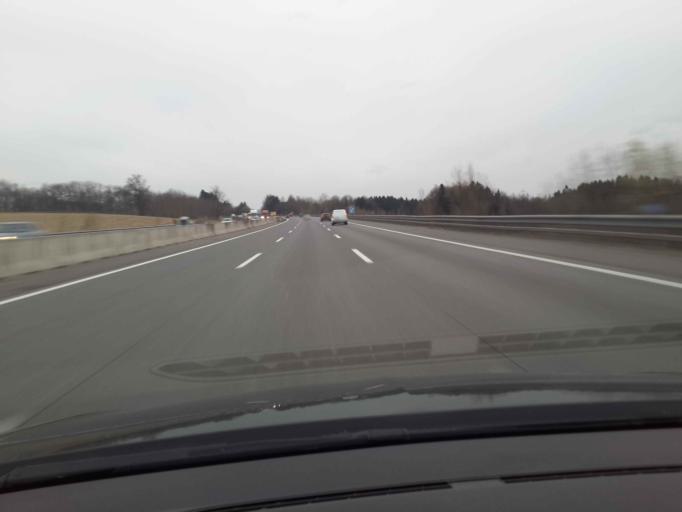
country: AT
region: Lower Austria
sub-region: Politischer Bezirk Amstetten
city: Sankt Georgen am Ybbsfelde
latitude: 48.1430
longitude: 14.9185
